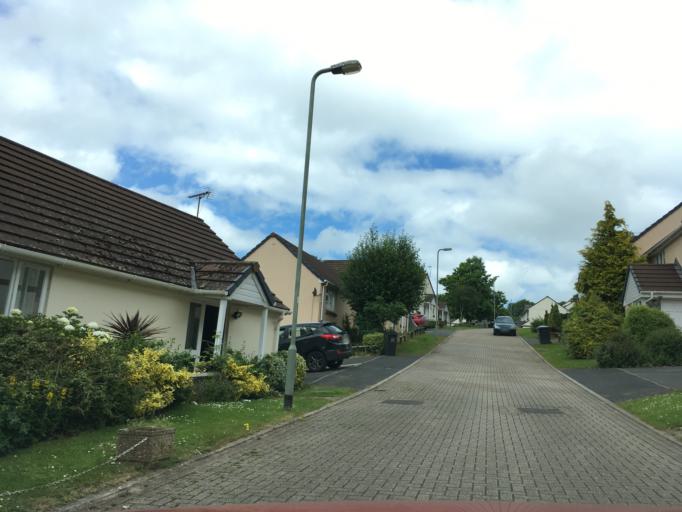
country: GB
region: England
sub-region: Devon
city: Dartmouth
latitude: 50.3560
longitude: -3.5917
